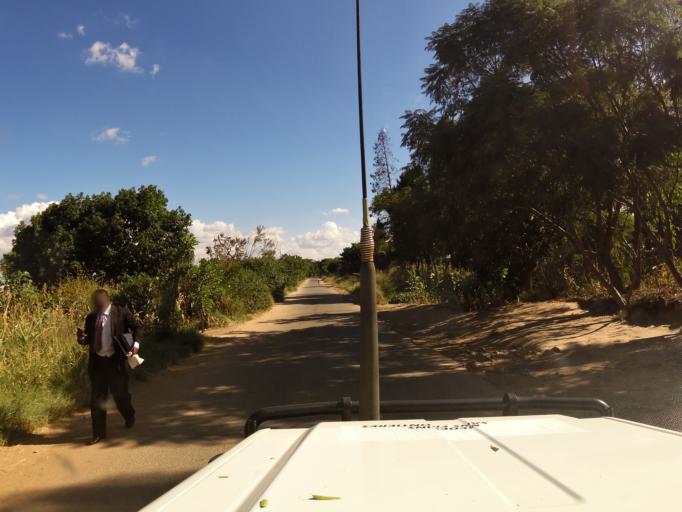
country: ZW
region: Harare
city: Epworth
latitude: -17.8764
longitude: 31.1319
